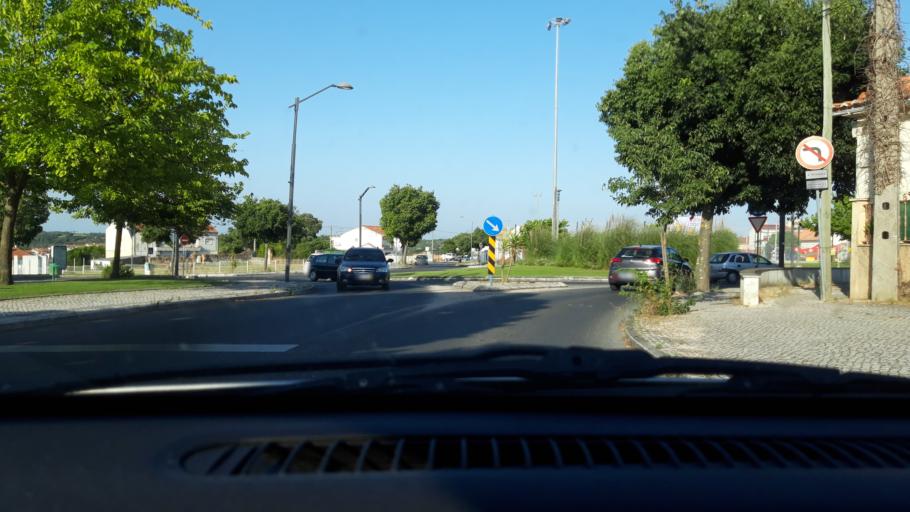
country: PT
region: Santarem
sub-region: Torres Novas
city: Torres Novas
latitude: 39.4778
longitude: -8.5468
